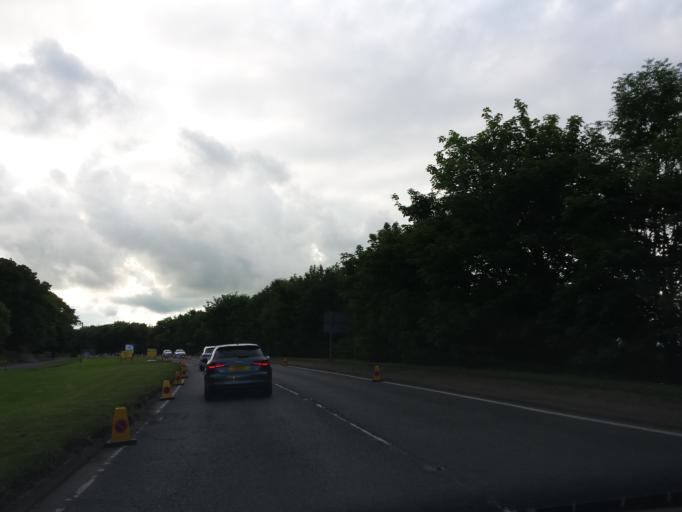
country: GB
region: Scotland
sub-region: Fife
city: Saint Andrews
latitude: 56.3469
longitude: -2.8205
